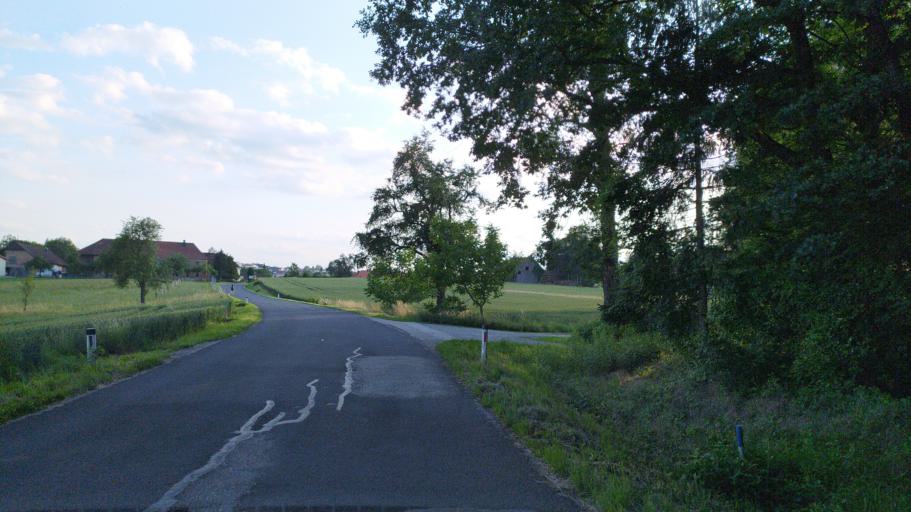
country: AT
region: Lower Austria
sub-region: Politischer Bezirk Amstetten
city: Strengberg
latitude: 48.1525
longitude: 14.6603
